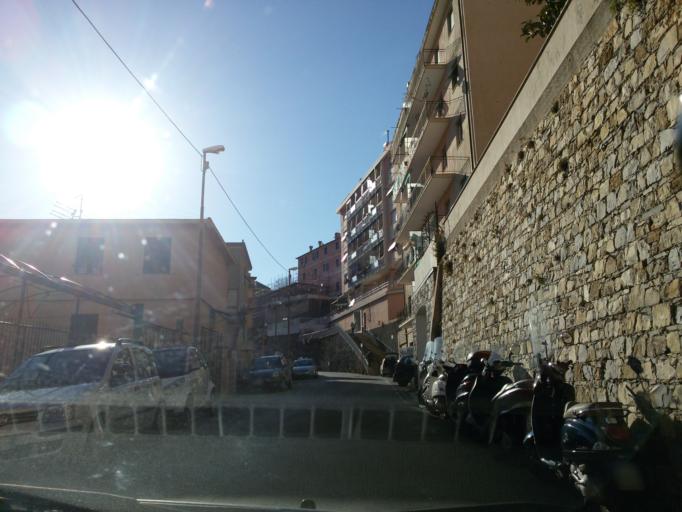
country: IT
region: Liguria
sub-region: Provincia di Genova
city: Genoa
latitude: 44.4228
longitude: 8.9738
